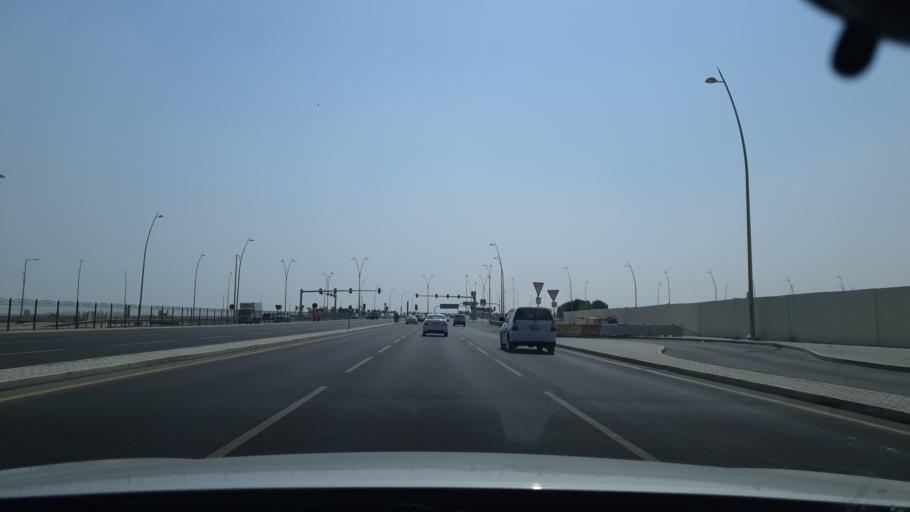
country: QA
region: Al Khawr
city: Al Khawr
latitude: 25.6654
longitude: 51.5008
